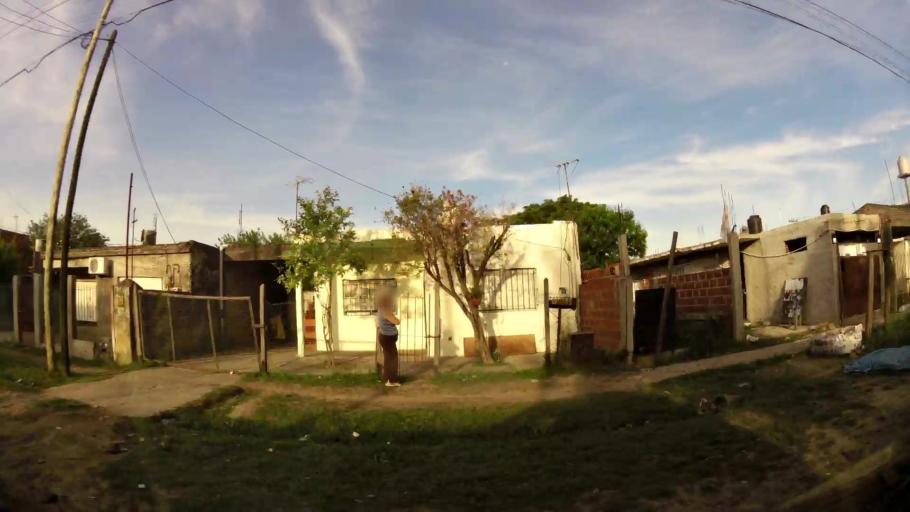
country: AR
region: Buenos Aires
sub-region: Partido de Almirante Brown
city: Adrogue
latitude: -34.7858
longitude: -58.3306
